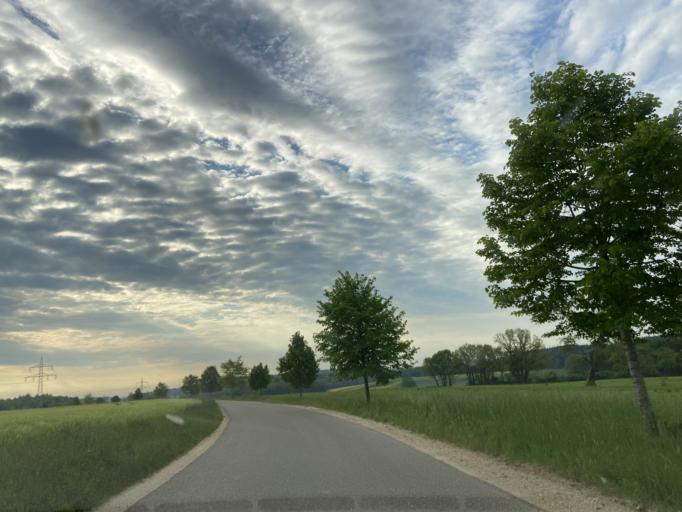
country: DE
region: Baden-Wuerttemberg
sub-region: Tuebingen Region
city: Scheer
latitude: 48.0981
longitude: 9.3058
